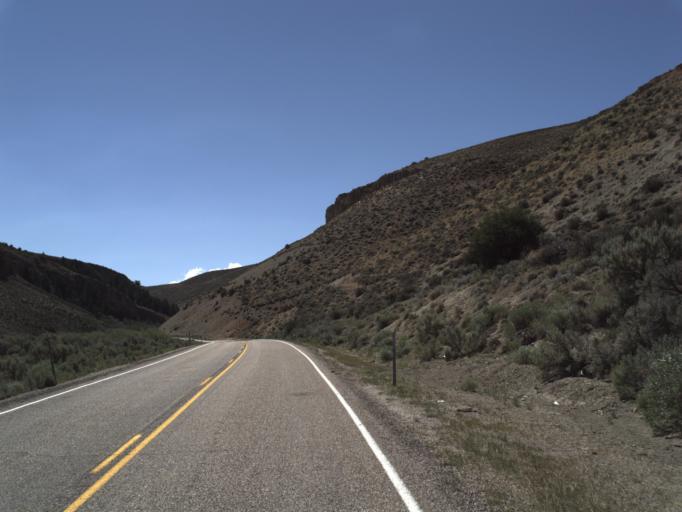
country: US
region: Utah
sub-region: Rich County
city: Randolph
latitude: 41.5027
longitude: -111.3048
